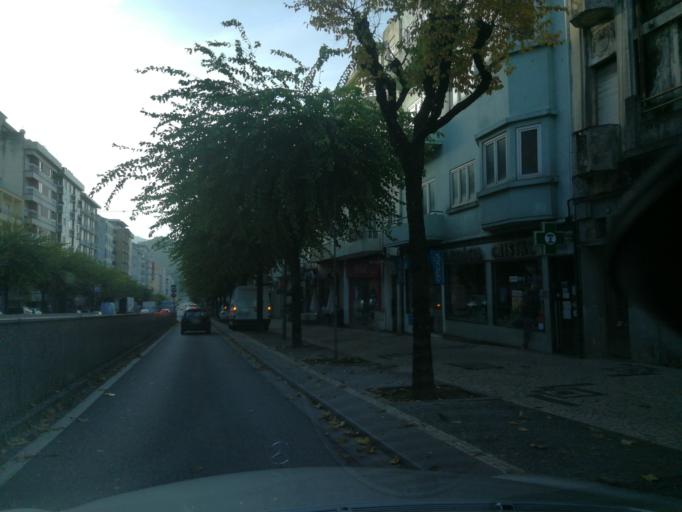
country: PT
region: Braga
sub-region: Braga
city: Braga
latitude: 41.5488
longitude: -8.4217
